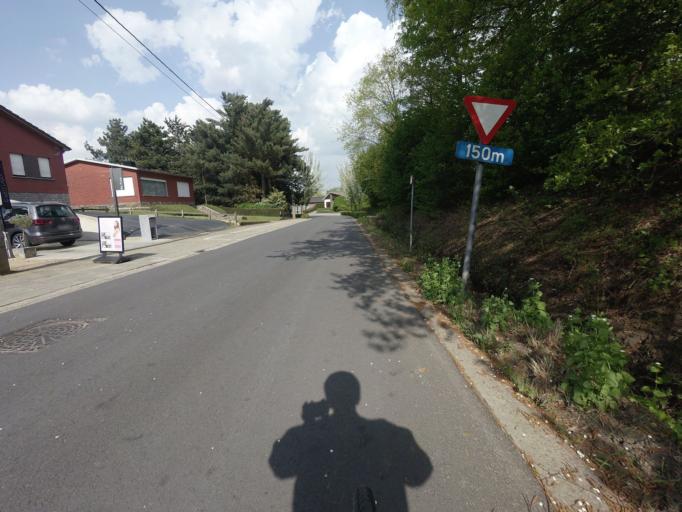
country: BE
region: Flanders
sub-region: Provincie Antwerpen
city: Putte
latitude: 51.0633
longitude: 4.6722
